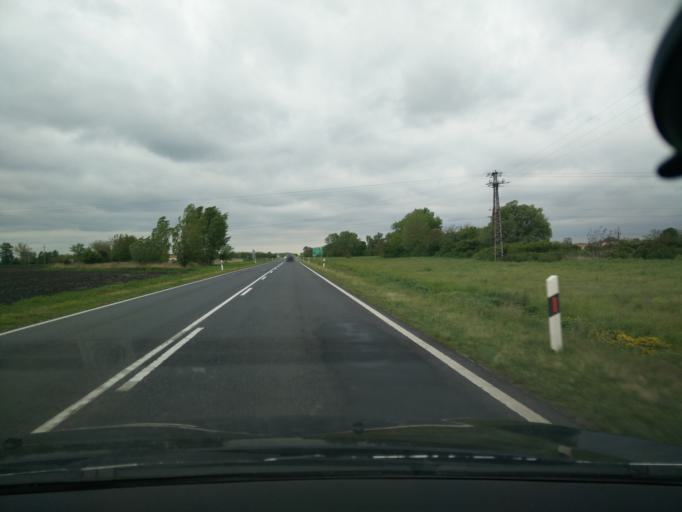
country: HU
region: Veszprem
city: Papa
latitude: 47.3369
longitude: 17.4359
